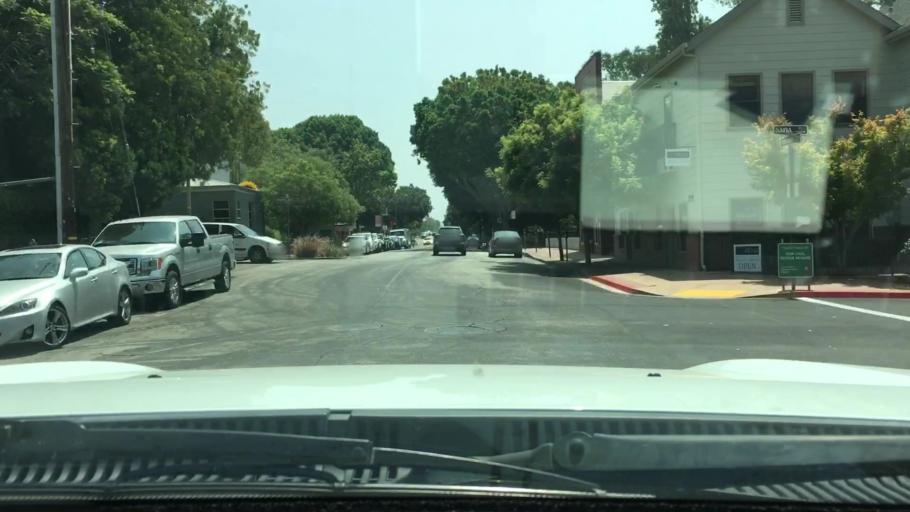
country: US
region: California
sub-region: San Luis Obispo County
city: San Luis Obispo
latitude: 35.2793
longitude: -120.6668
